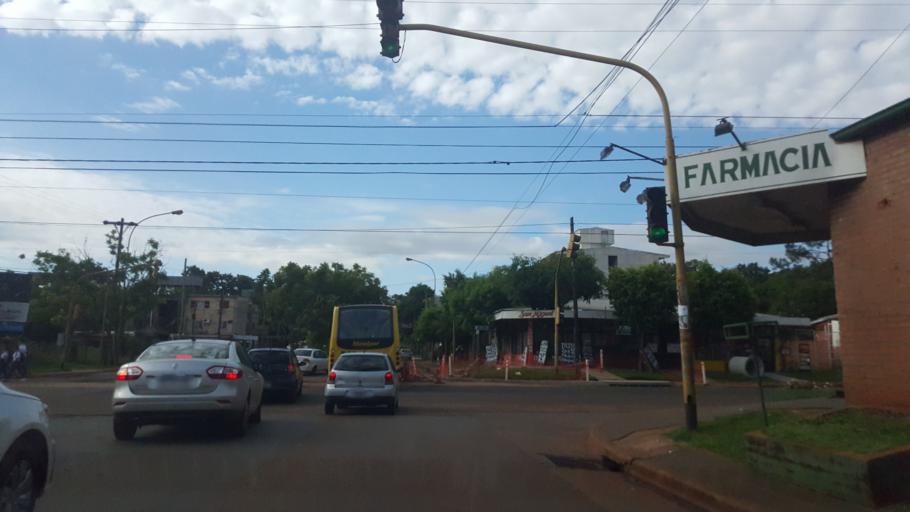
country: AR
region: Misiones
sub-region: Departamento de Capital
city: Posadas
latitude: -27.3709
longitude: -55.9321
